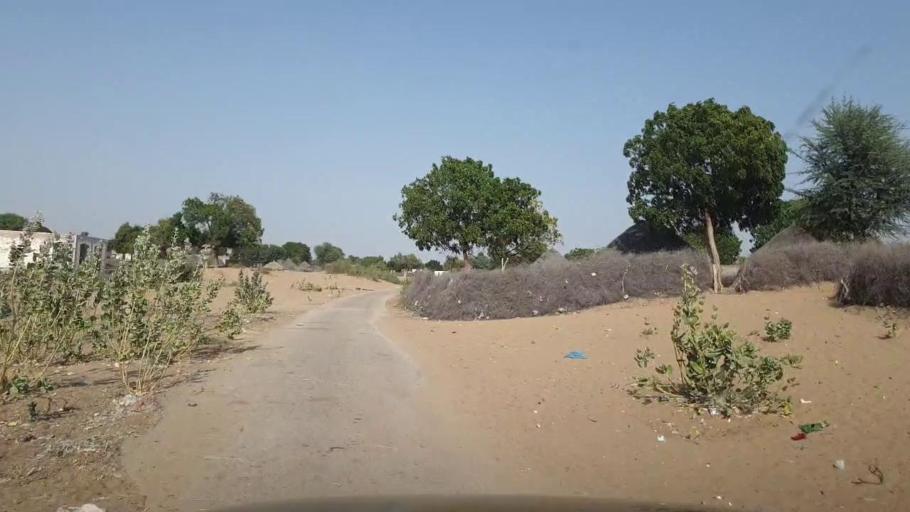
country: PK
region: Sindh
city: Islamkot
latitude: 25.1324
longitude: 70.4573
